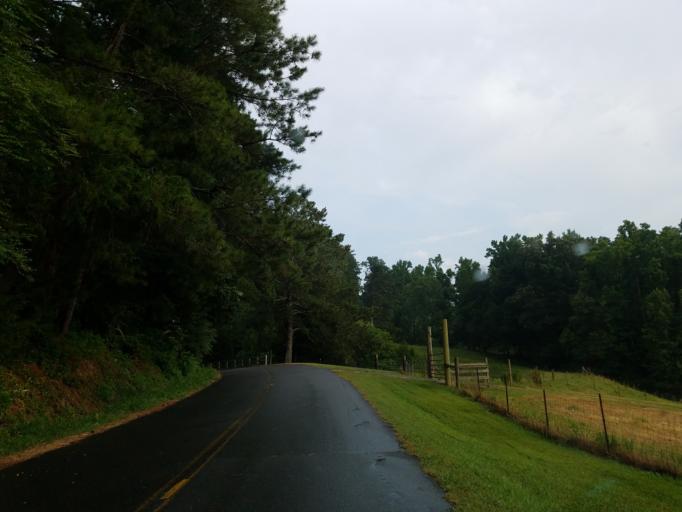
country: US
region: Georgia
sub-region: Bartow County
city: Rydal
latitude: 34.3895
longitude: -84.6572
